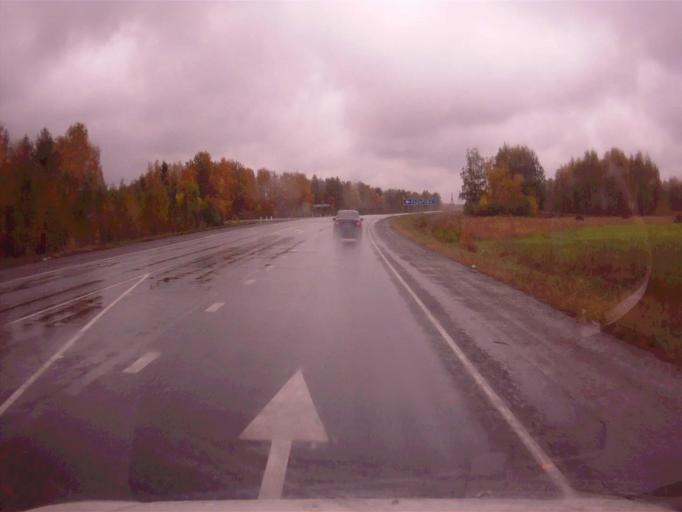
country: RU
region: Chelyabinsk
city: Roshchino
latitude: 55.3997
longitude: 61.0763
